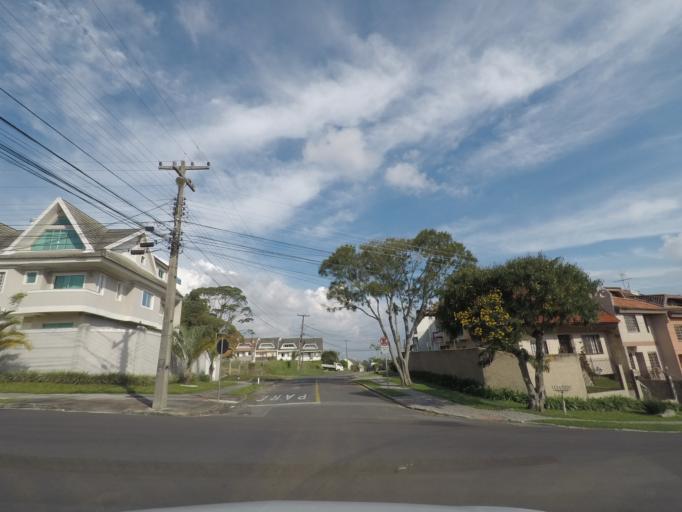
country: BR
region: Parana
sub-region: Pinhais
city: Pinhais
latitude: -25.4657
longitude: -49.2277
